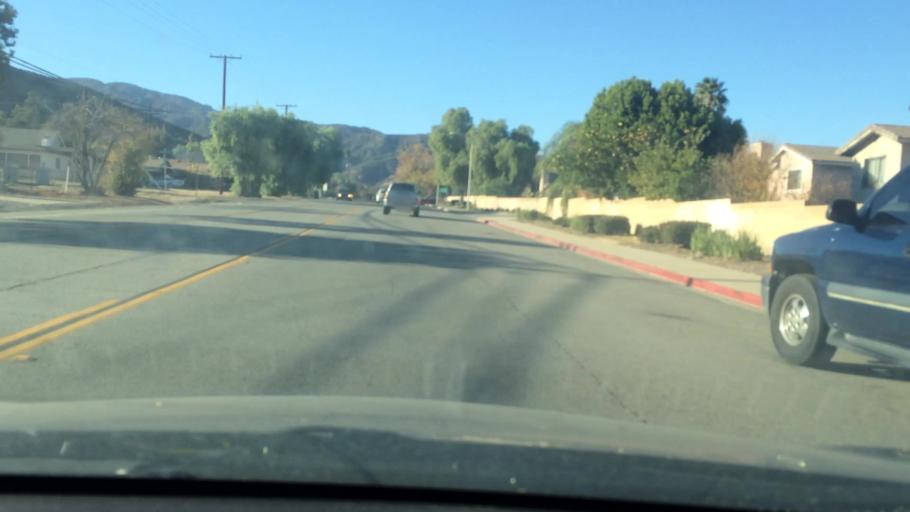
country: US
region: California
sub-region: Riverside County
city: Lakeland Village
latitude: 33.6669
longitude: -117.3895
